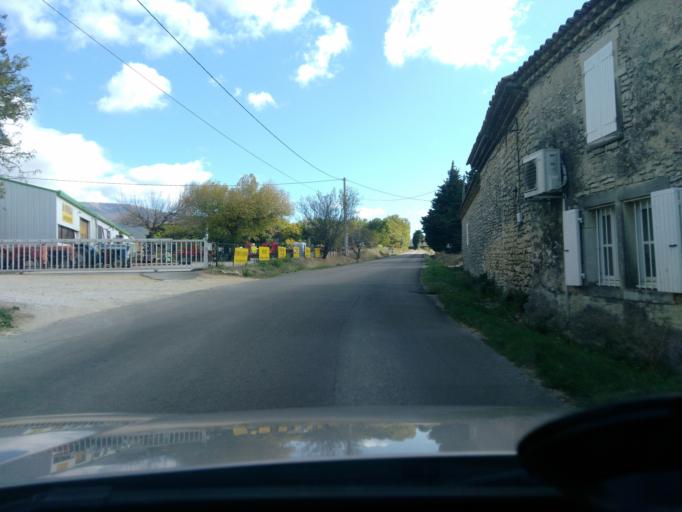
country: FR
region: Rhone-Alpes
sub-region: Departement de la Drome
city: Taulignan
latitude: 44.4454
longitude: 4.9857
